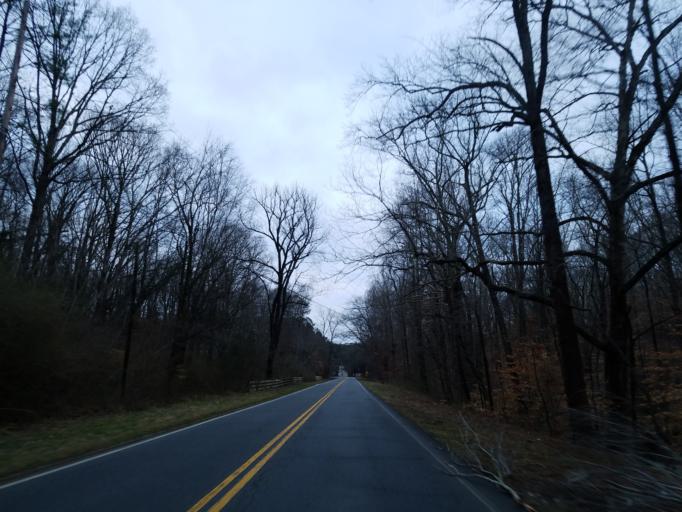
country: US
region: Georgia
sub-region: Bartow County
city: Emerson
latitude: 34.0916
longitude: -84.7308
